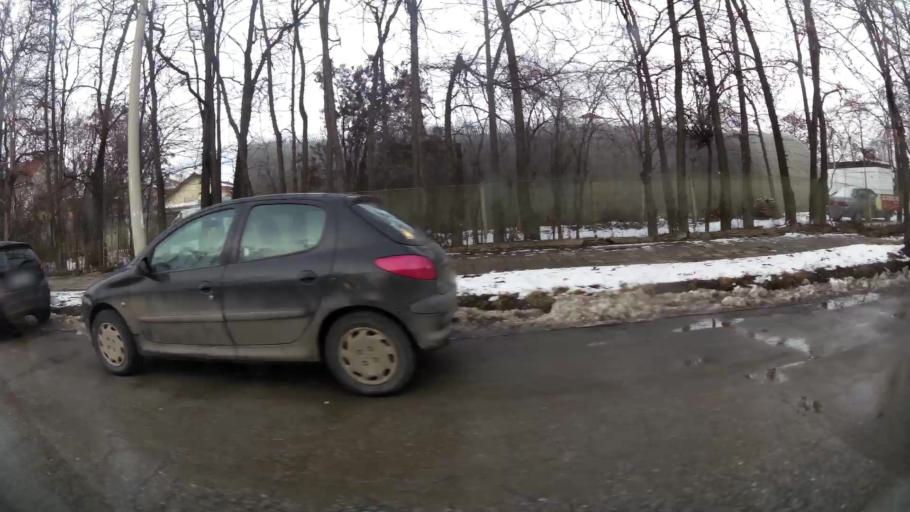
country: BG
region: Sofia-Capital
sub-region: Stolichna Obshtina
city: Sofia
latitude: 42.7185
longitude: 23.3375
